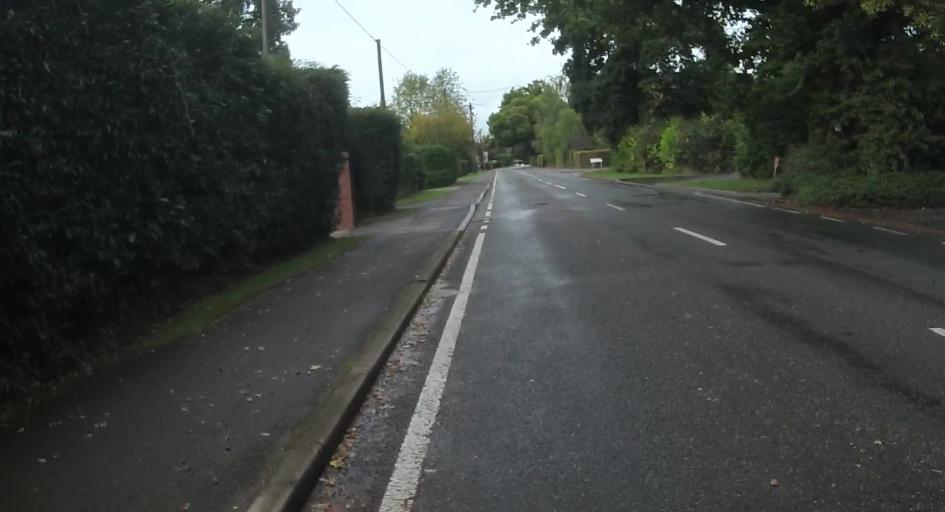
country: GB
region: England
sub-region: Hampshire
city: Tadley
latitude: 51.3514
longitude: -1.1675
